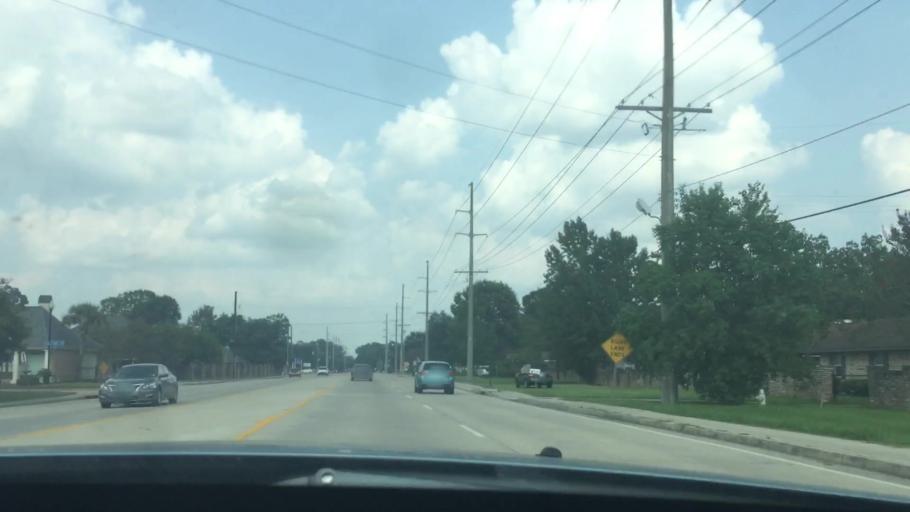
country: US
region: Louisiana
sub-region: East Baton Rouge Parish
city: Westminster
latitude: 30.4389
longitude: -91.0502
